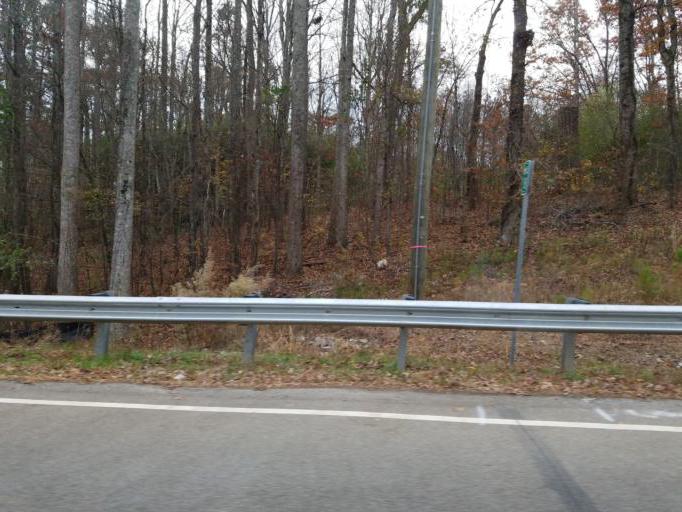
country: US
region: Georgia
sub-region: Cherokee County
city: Canton
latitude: 34.2126
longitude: -84.5291
